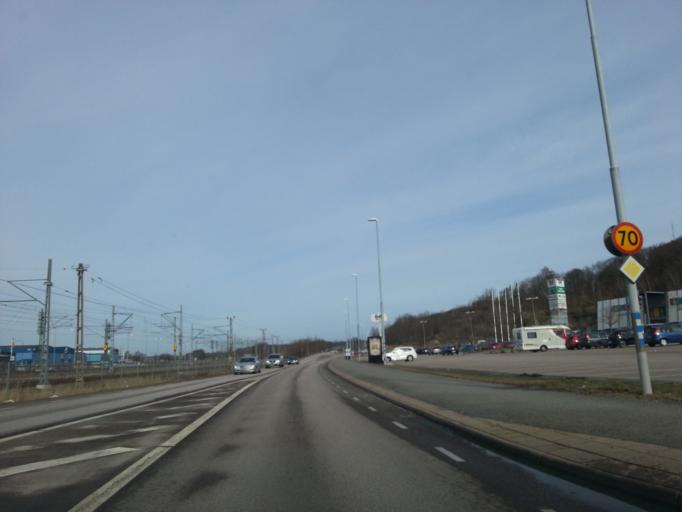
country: SE
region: Vaestra Goetaland
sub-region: Goteborg
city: Eriksbo
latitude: 57.7432
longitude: 12.0072
